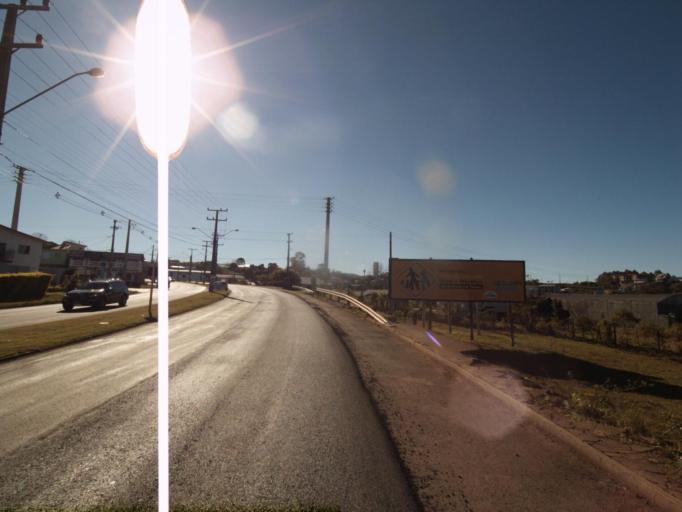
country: AR
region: Misiones
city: Bernardo de Irigoyen
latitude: -26.7386
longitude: -53.5013
